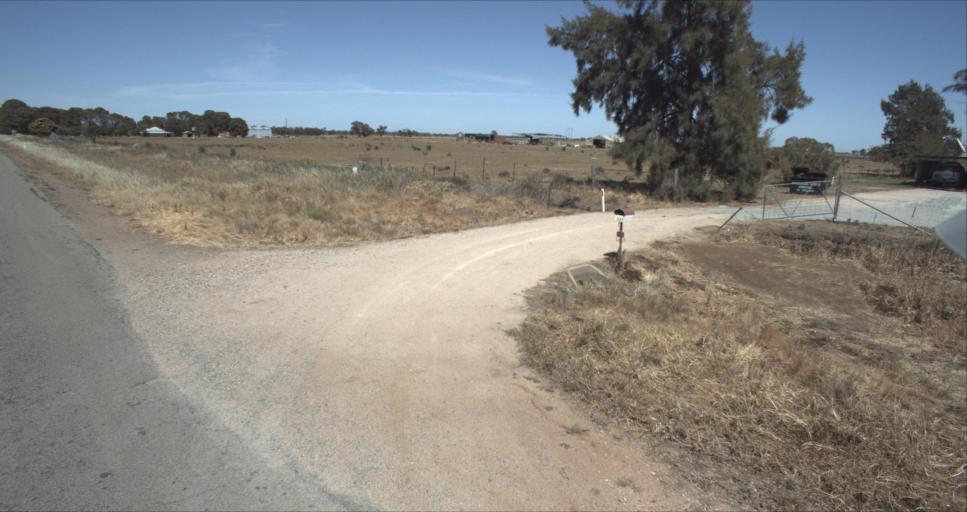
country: AU
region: New South Wales
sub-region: Leeton
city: Leeton
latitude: -34.5689
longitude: 146.3110
